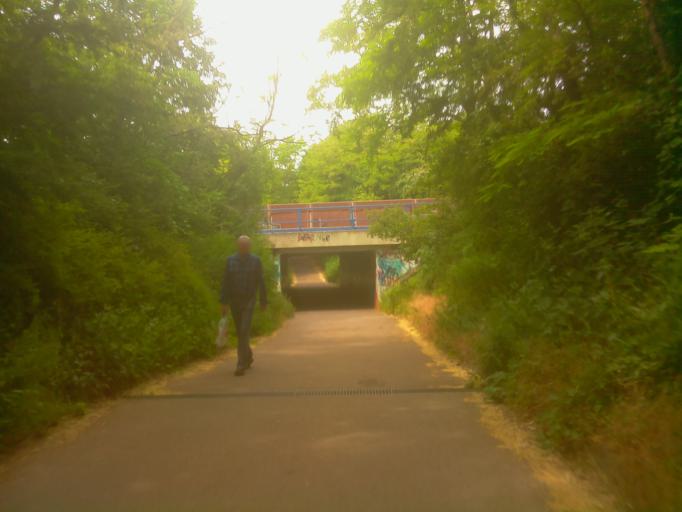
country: DE
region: Baden-Wuerttemberg
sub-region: Karlsruhe Region
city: Mannheim
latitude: 49.5472
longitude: 8.4836
